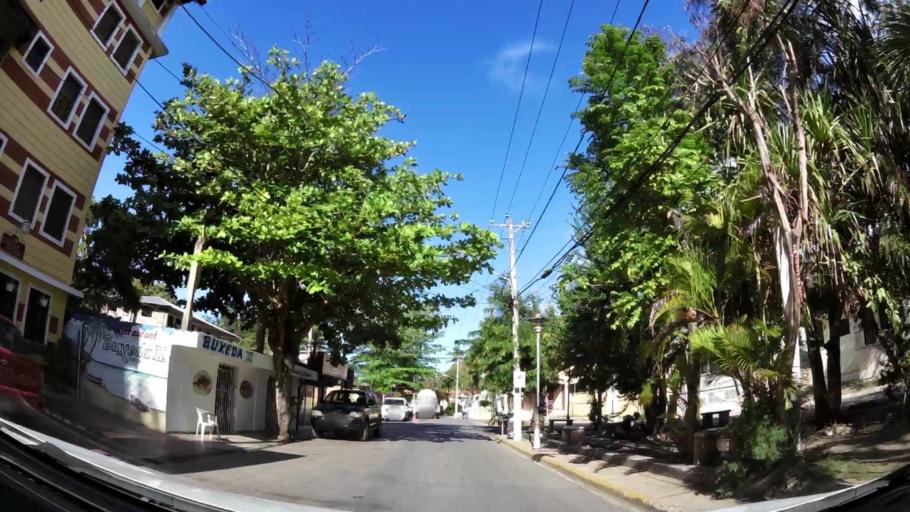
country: DO
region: Santo Domingo
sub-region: Santo Domingo
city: Boca Chica
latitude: 18.4483
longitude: -69.6118
